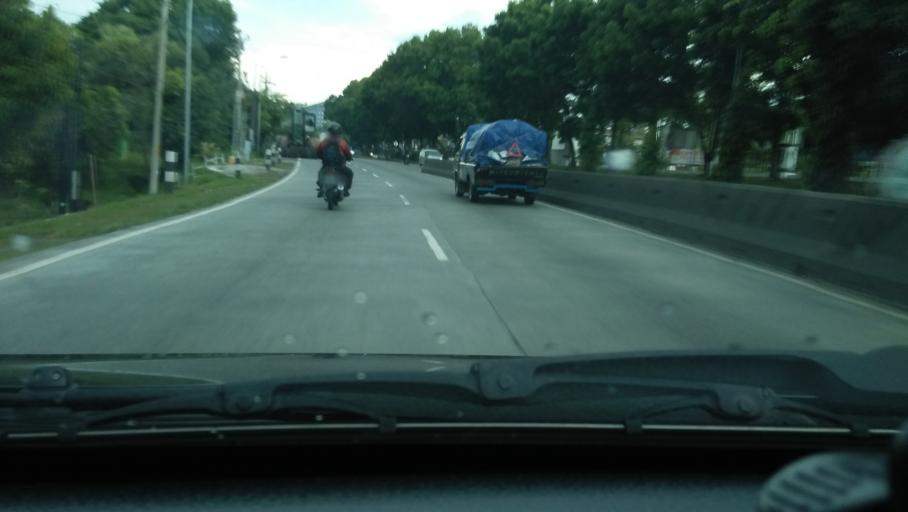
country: ID
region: Central Java
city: Ungaran
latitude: -7.0912
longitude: 110.4088
